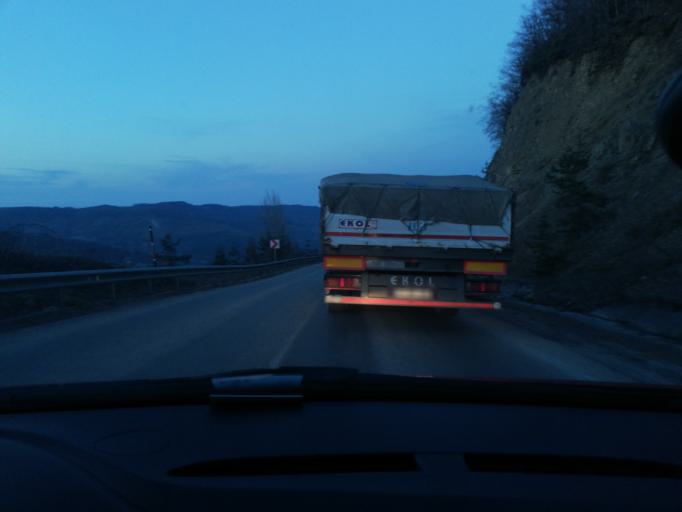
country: TR
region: Kastamonu
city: Inebolu
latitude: 41.9157
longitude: 33.7267
